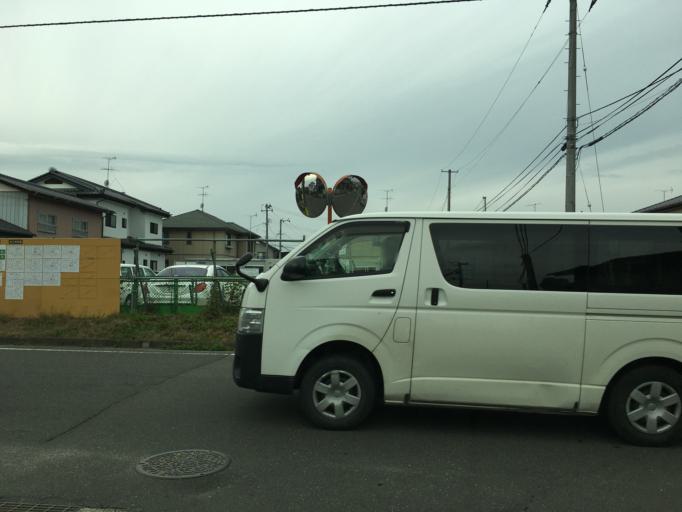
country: JP
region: Fukushima
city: Hobaramachi
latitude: 37.8240
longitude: 140.5032
